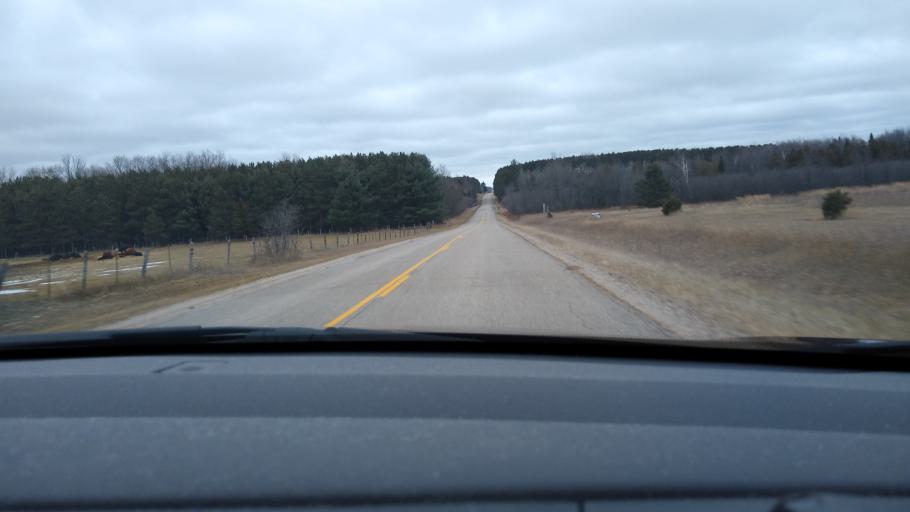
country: US
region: Michigan
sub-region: Missaukee County
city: Lake City
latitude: 44.2529
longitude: -85.0536
